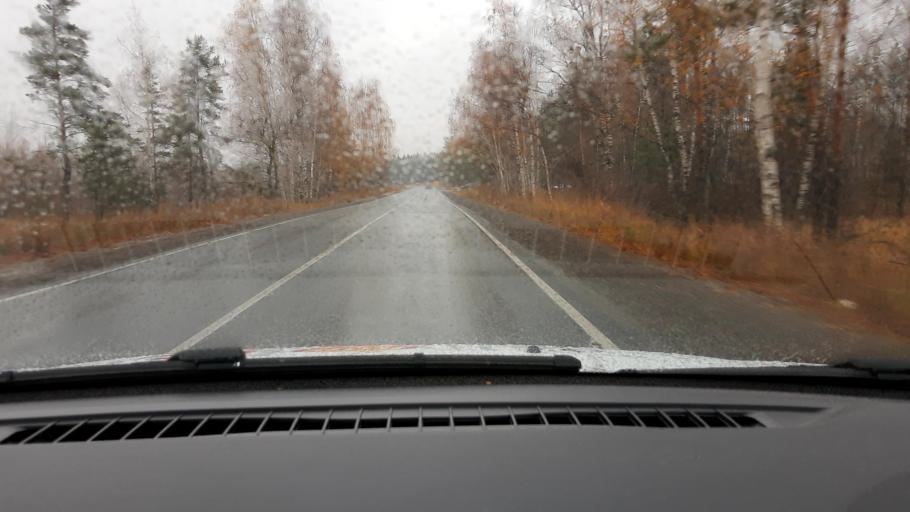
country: RU
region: Nizjnij Novgorod
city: Babino
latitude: 56.2954
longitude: 43.5976
